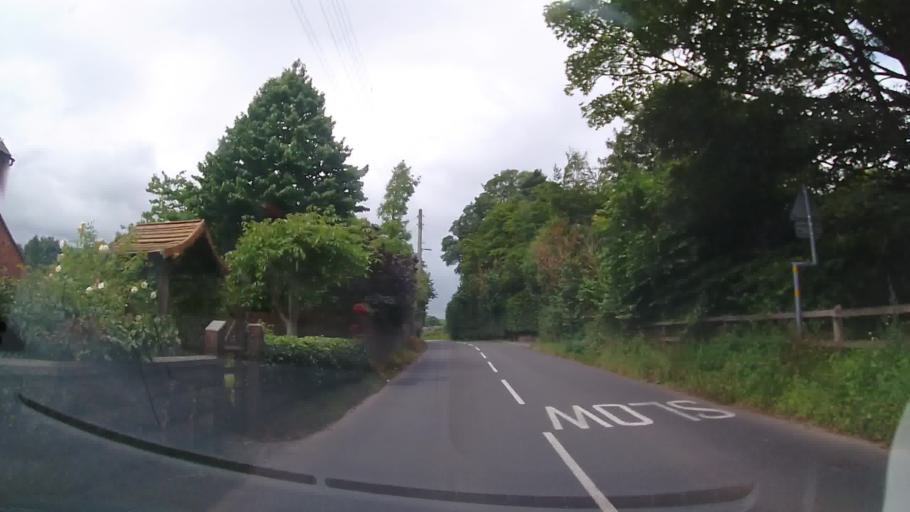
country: GB
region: England
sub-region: Shropshire
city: Wem
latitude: 52.8561
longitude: -2.7337
